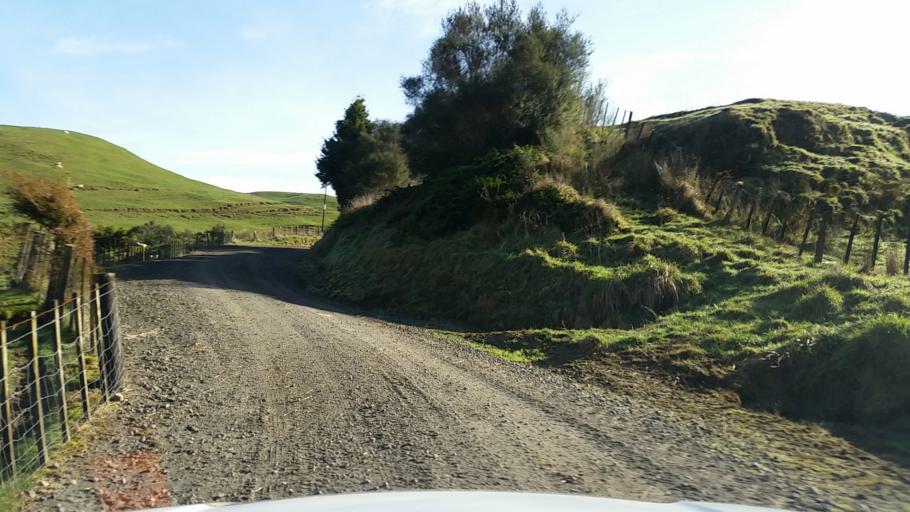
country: NZ
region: Taranaki
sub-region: South Taranaki District
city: Eltham
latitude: -39.3164
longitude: 174.5341
